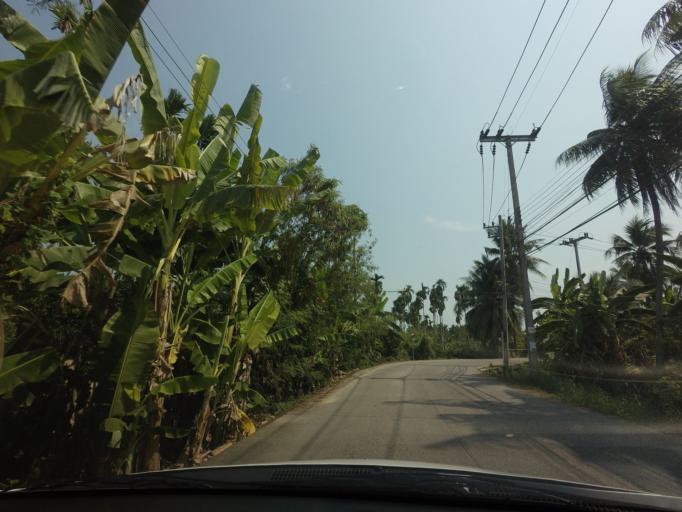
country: TH
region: Nakhon Pathom
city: Sam Phran
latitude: 13.7656
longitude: 100.2586
